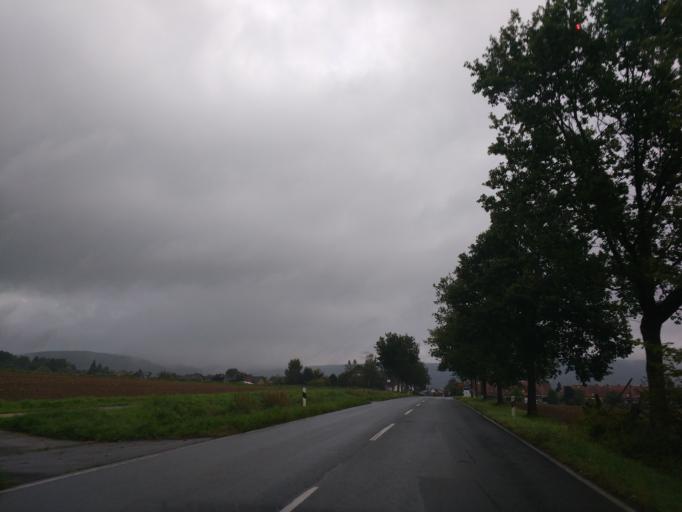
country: DE
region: Lower Saxony
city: Bad Pyrmont
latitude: 51.9760
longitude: 9.2318
